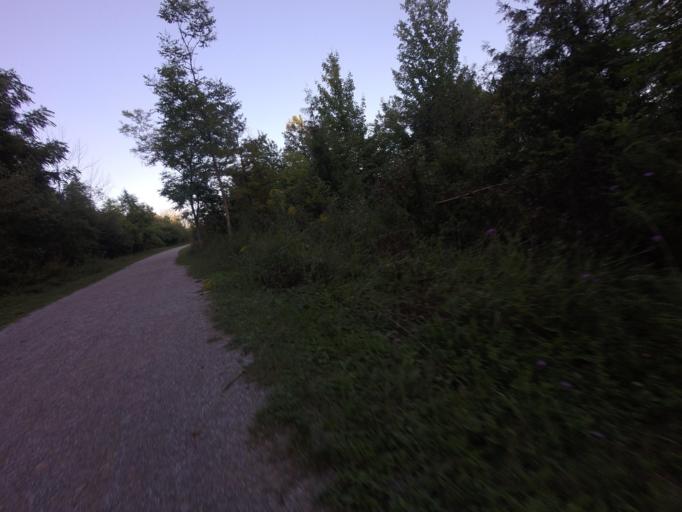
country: CA
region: Ontario
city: Goderich
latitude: 43.7598
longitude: -81.7085
